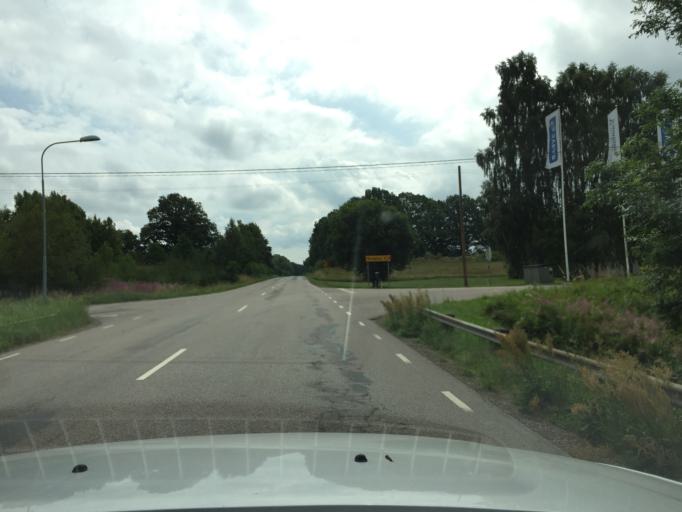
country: SE
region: Skane
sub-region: Hassleholms Kommun
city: Sosdala
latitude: 56.0296
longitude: 13.6856
